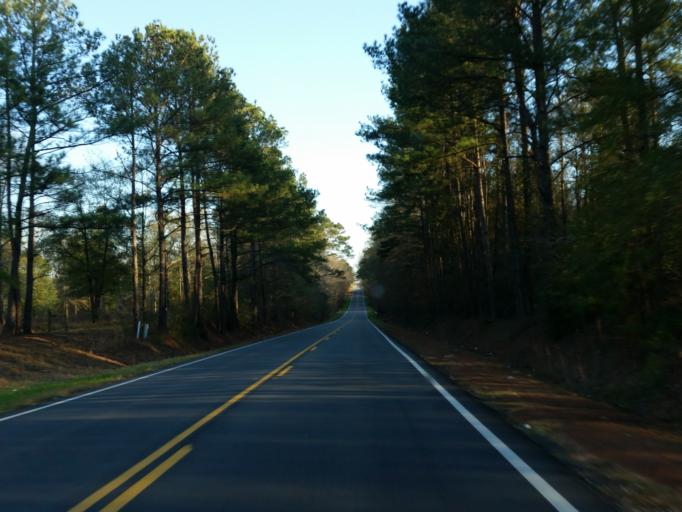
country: US
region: Georgia
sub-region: Dooly County
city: Unadilla
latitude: 32.3209
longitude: -83.7776
